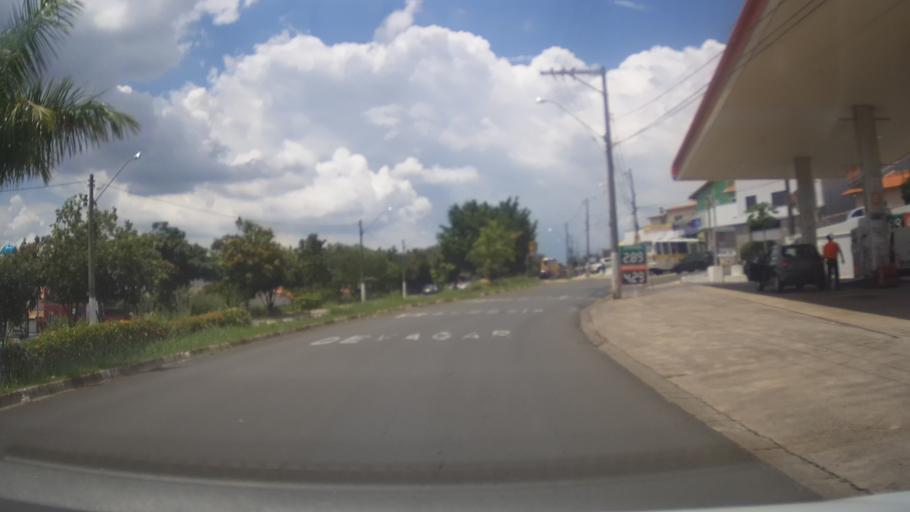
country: BR
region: Sao Paulo
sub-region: Valinhos
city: Valinhos
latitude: -22.9464
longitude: -46.9978
